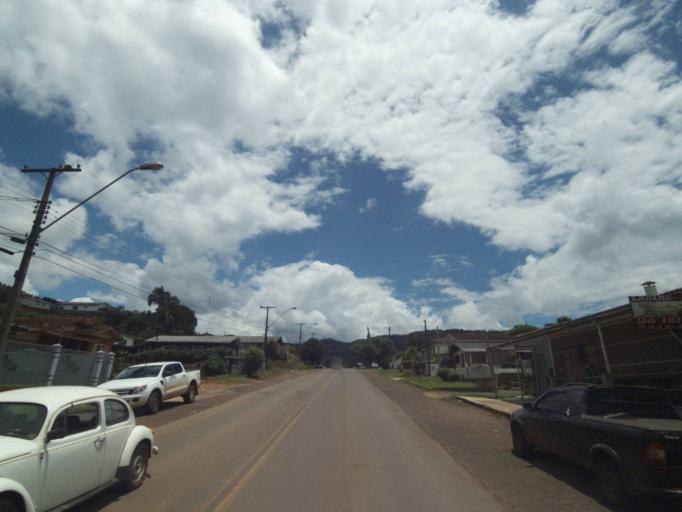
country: BR
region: Parana
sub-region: Pinhao
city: Pinhao
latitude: -26.1569
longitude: -51.5583
